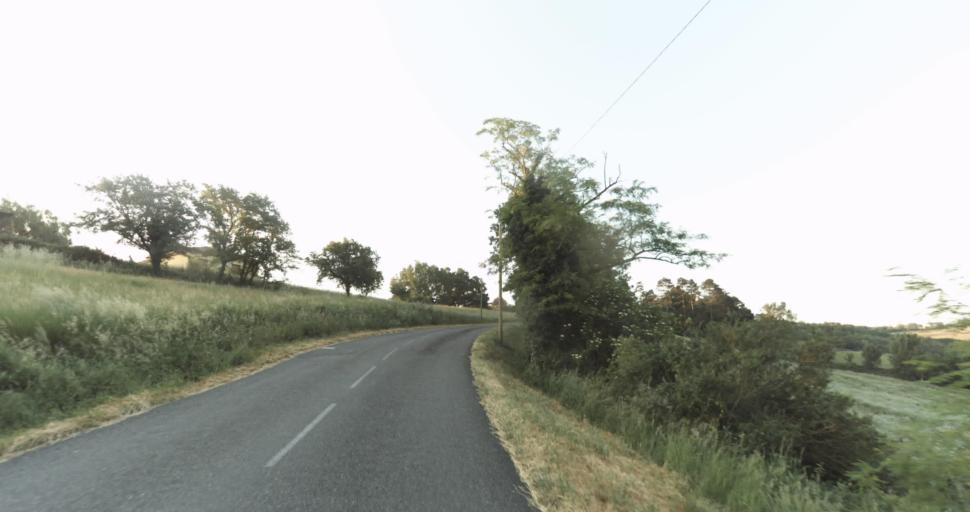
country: FR
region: Midi-Pyrenees
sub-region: Departement du Gers
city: Pujaudran
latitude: 43.6112
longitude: 1.1587
